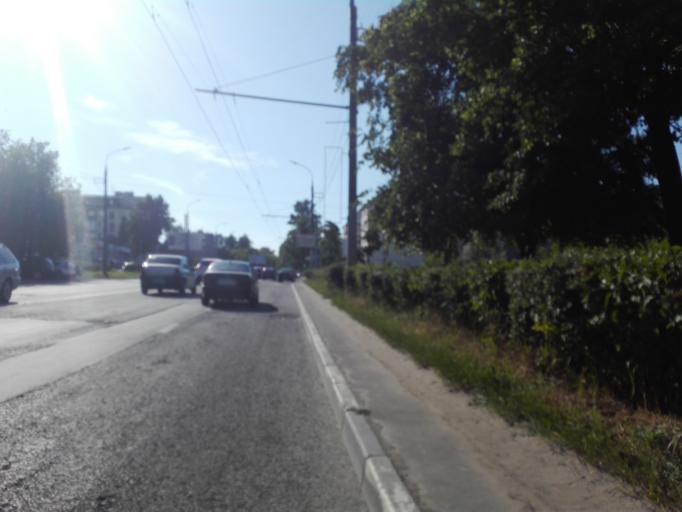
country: RU
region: Orjol
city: Orel
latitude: 52.9805
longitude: 36.0724
